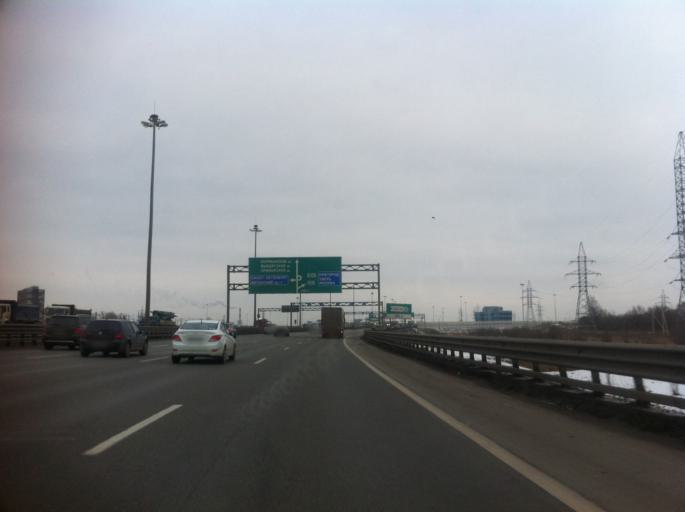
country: RU
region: St.-Petersburg
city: Shushary
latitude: 59.8149
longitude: 30.3565
